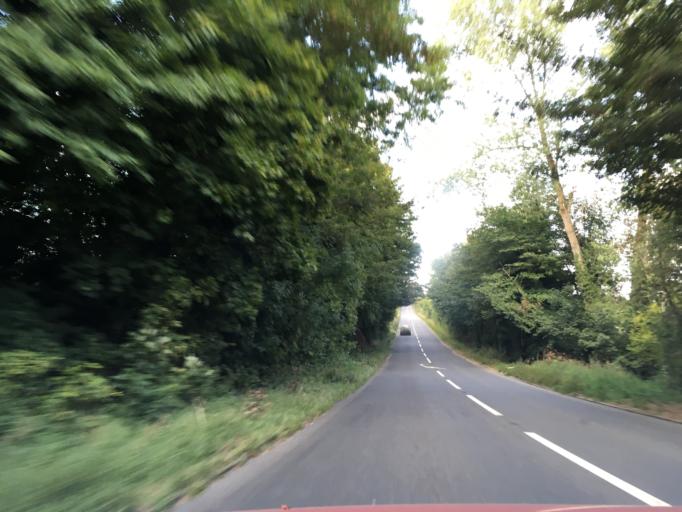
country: GB
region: England
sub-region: Gloucestershire
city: Northleach
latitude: 51.8431
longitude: -1.8291
